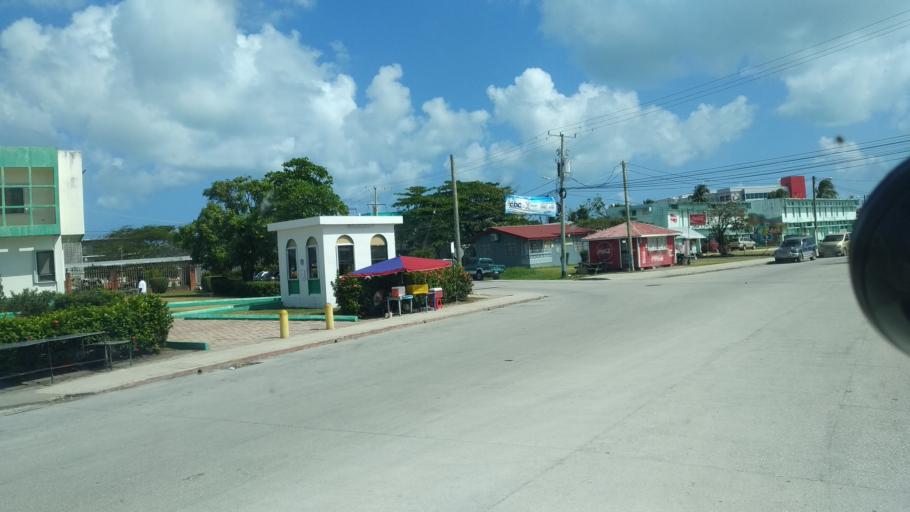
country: BZ
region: Belize
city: Belize City
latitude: 17.5063
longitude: -88.1963
